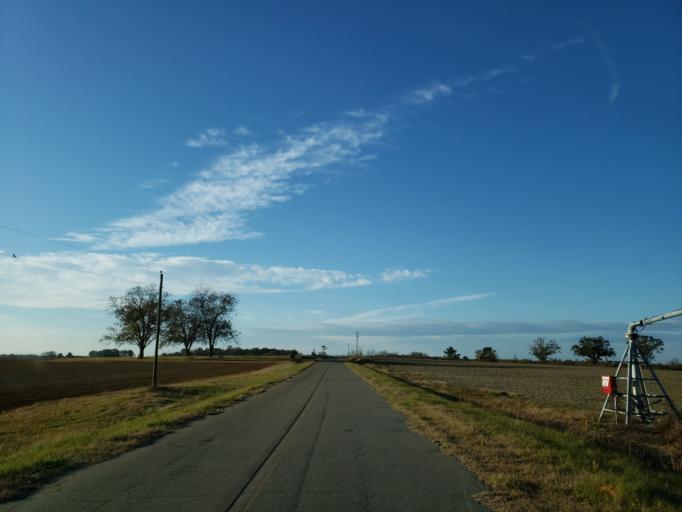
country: US
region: Georgia
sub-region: Dooly County
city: Unadilla
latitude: 32.2042
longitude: -83.7699
